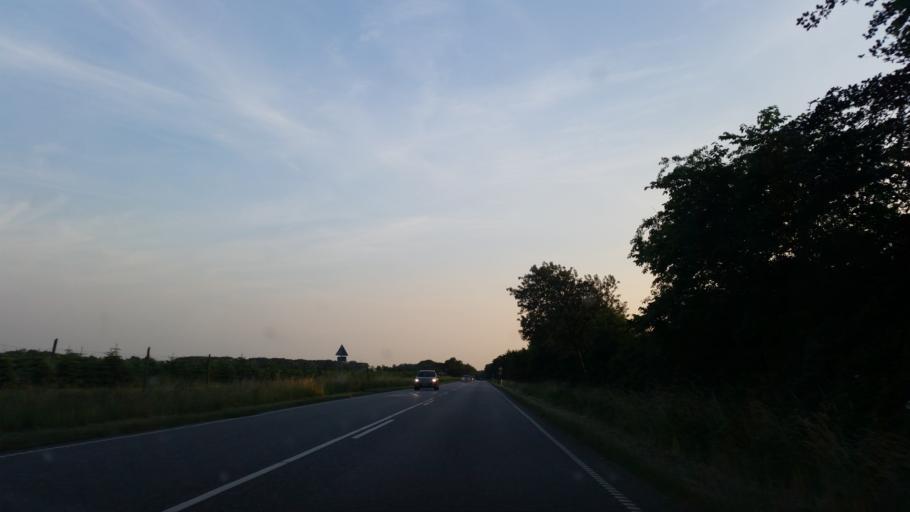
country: DK
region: South Denmark
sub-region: Kolding Kommune
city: Lunderskov
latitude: 55.5047
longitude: 9.3239
